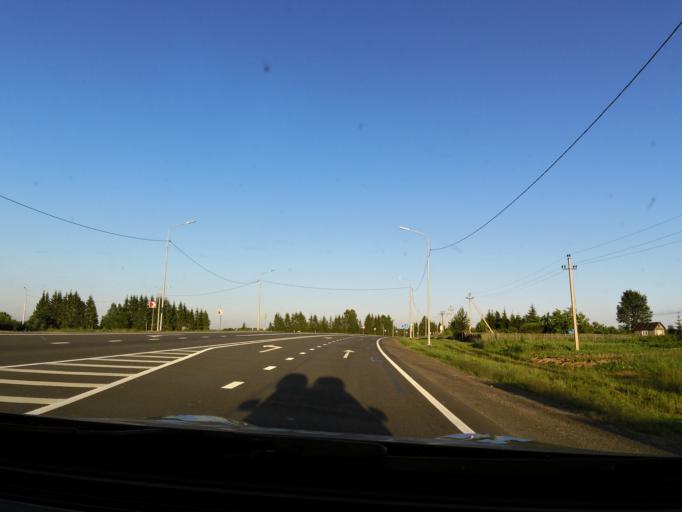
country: RU
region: Vologda
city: Gryazovets
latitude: 58.7956
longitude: 40.2635
